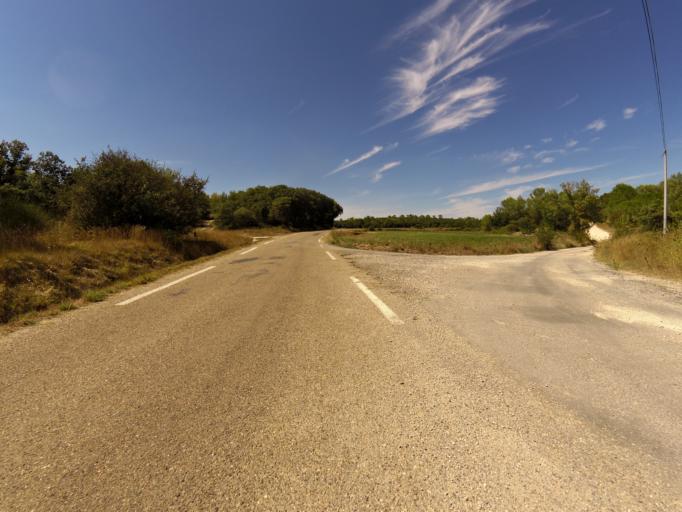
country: FR
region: Languedoc-Roussillon
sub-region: Departement du Gard
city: Sommieres
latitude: 43.8451
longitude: 4.0554
